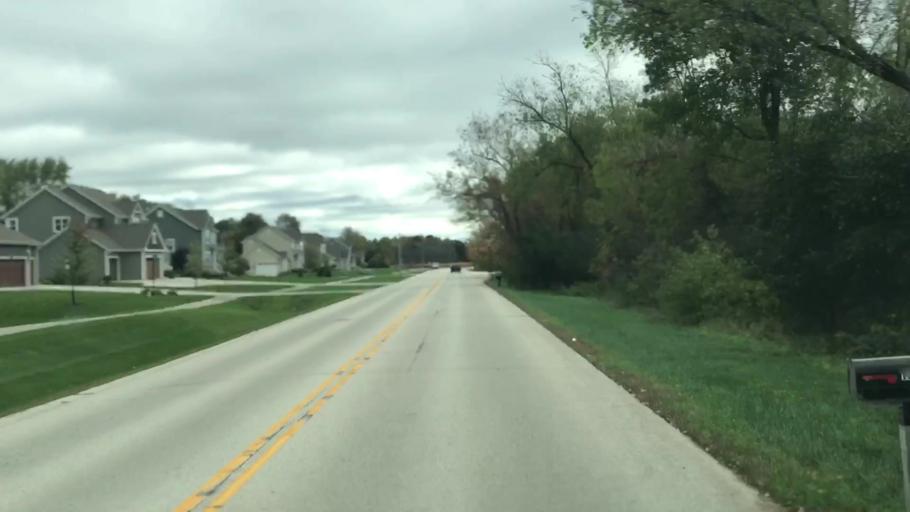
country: US
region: Wisconsin
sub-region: Waukesha County
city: Brookfield
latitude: 43.0757
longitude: -88.1304
